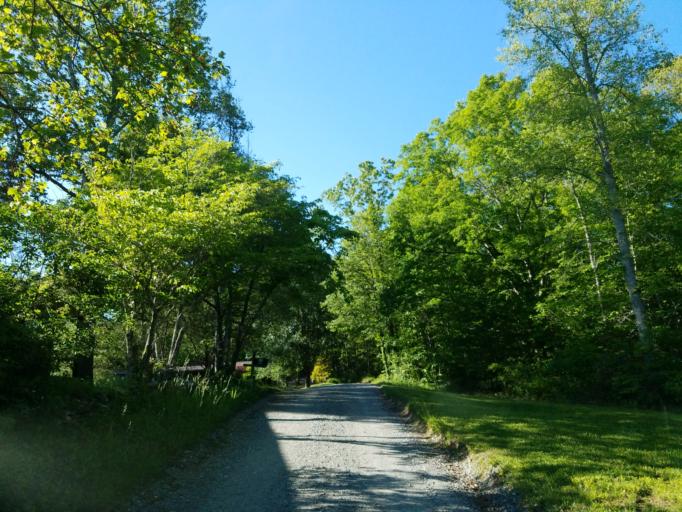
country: US
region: Georgia
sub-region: Fannin County
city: Blue Ridge
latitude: 34.8510
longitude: -84.1952
